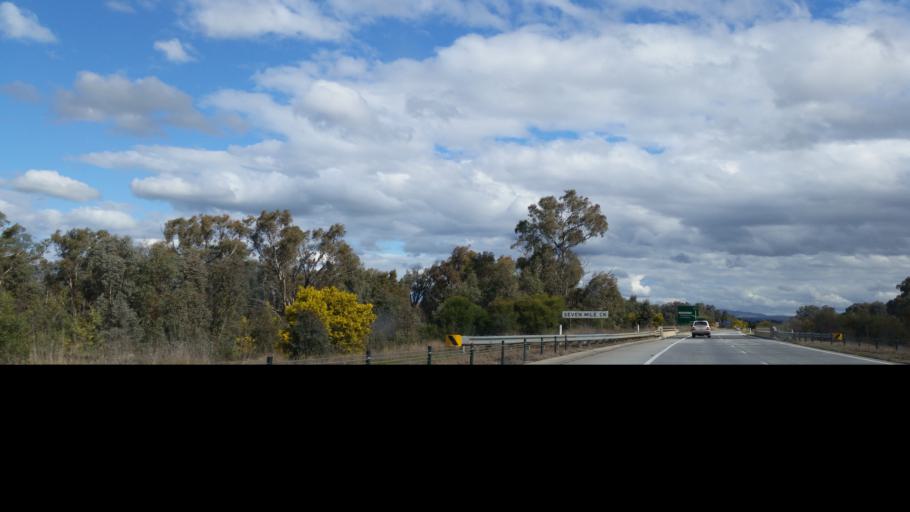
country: AU
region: New South Wales
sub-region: Albury Municipality
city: Lavington
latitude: -36.0167
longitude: 146.9854
